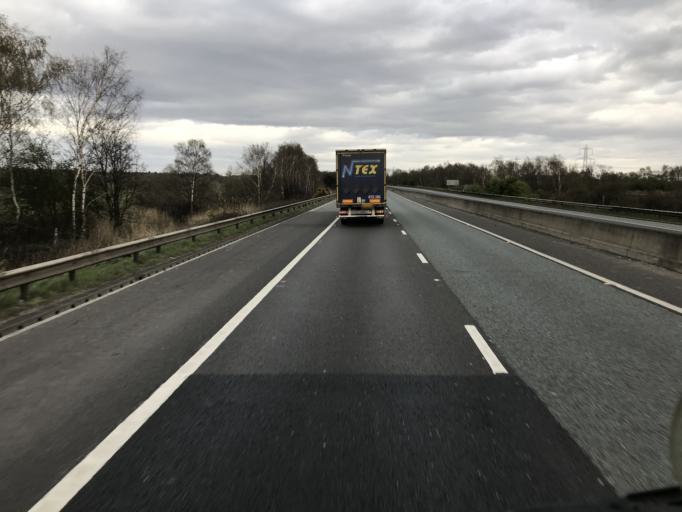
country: GB
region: England
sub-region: Doncaster
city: Rossington
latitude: 53.4879
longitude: -1.0919
